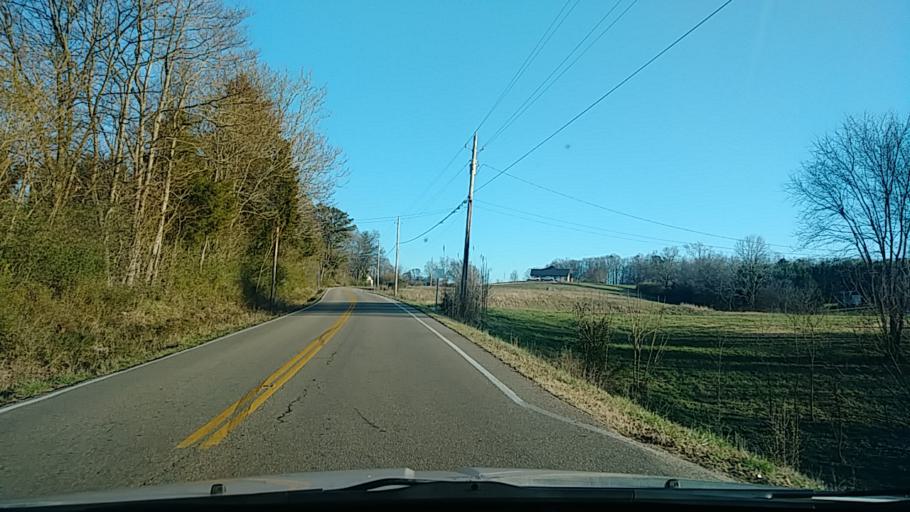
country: US
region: Tennessee
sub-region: Hamblen County
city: Morristown
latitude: 36.2033
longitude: -83.4044
